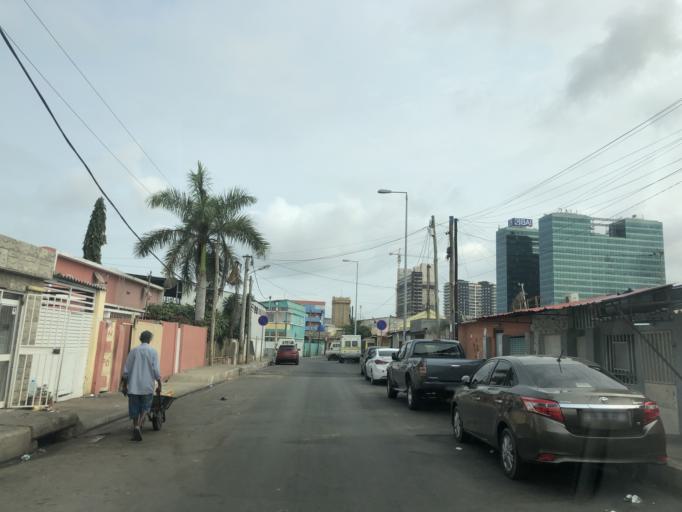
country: AO
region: Luanda
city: Luanda
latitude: -8.8409
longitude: 13.2354
